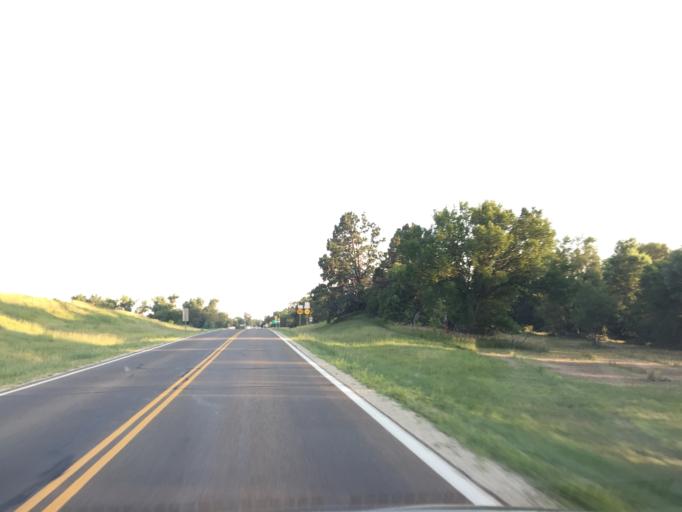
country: US
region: Kansas
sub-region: Ellsworth County
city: Ellsworth
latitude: 38.7439
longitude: -98.2252
